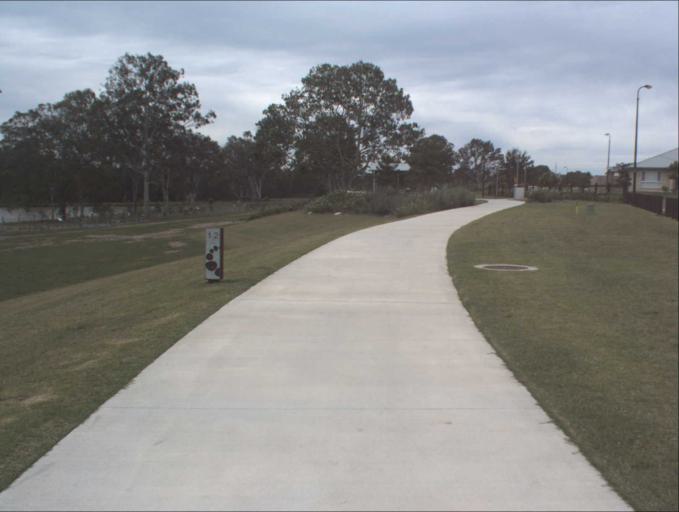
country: AU
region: Queensland
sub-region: Logan
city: Logan Reserve
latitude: -27.7090
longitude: 153.1105
